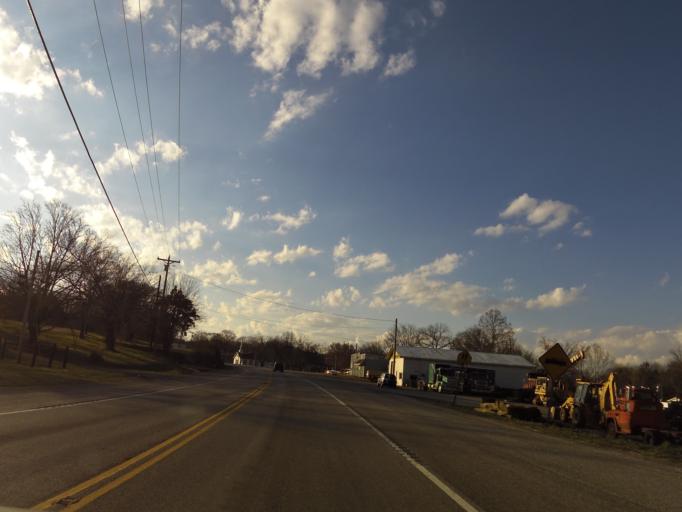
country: US
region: Tennessee
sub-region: Smith County
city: Carthage
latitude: 36.2628
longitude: -86.0526
